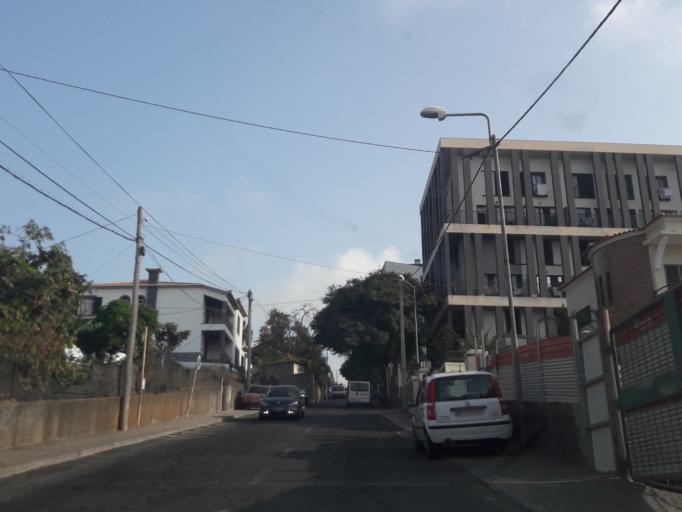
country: PT
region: Madeira
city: Camara de Lobos
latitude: 32.6483
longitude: -16.9419
